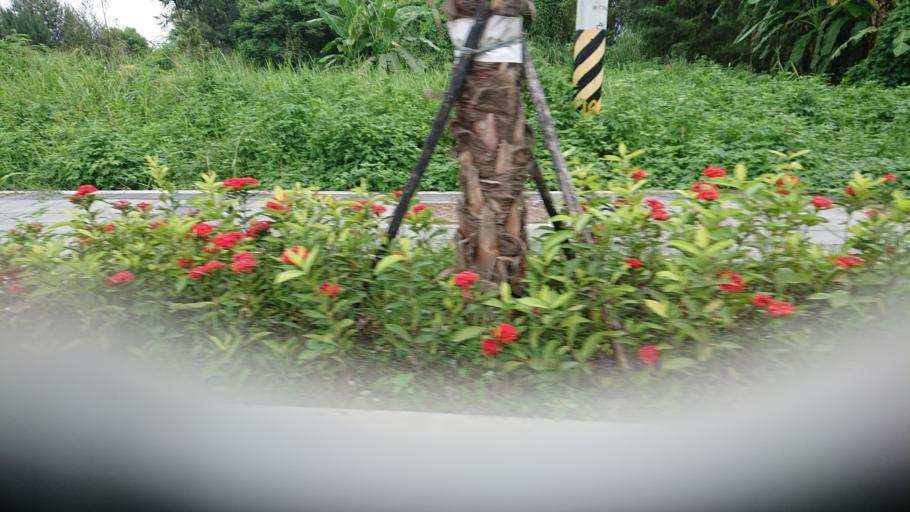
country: TW
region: Taiwan
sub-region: Hualien
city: Hualian
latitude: 23.9604
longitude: 121.6039
